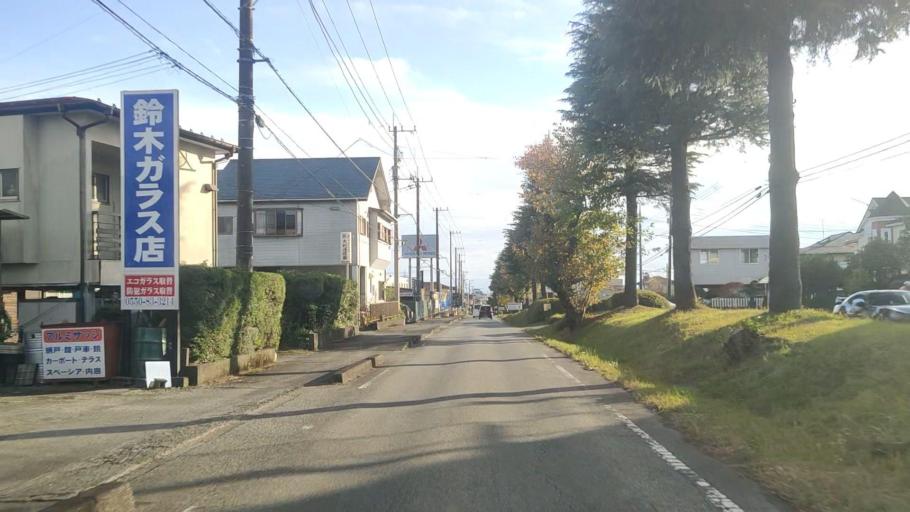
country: JP
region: Shizuoka
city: Gotemba
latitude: 35.2910
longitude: 138.9283
